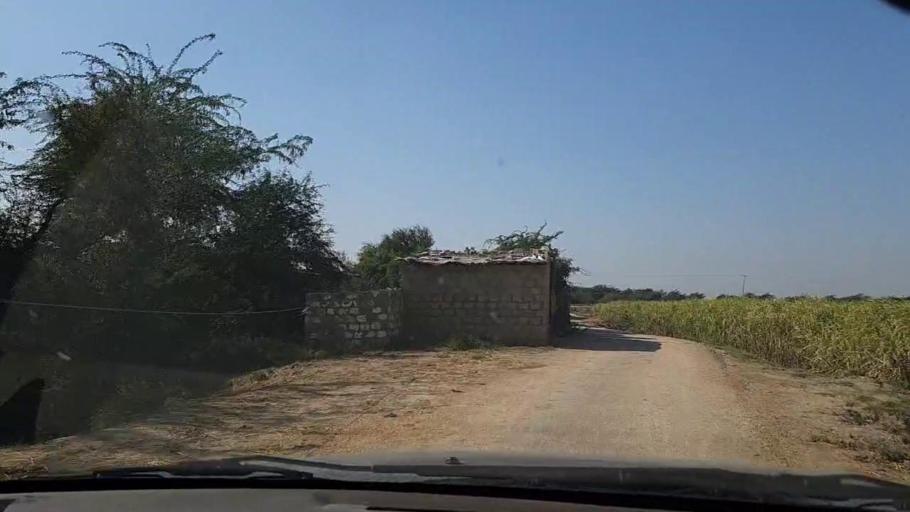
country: PK
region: Sindh
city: Thatta
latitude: 24.6033
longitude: 68.0526
